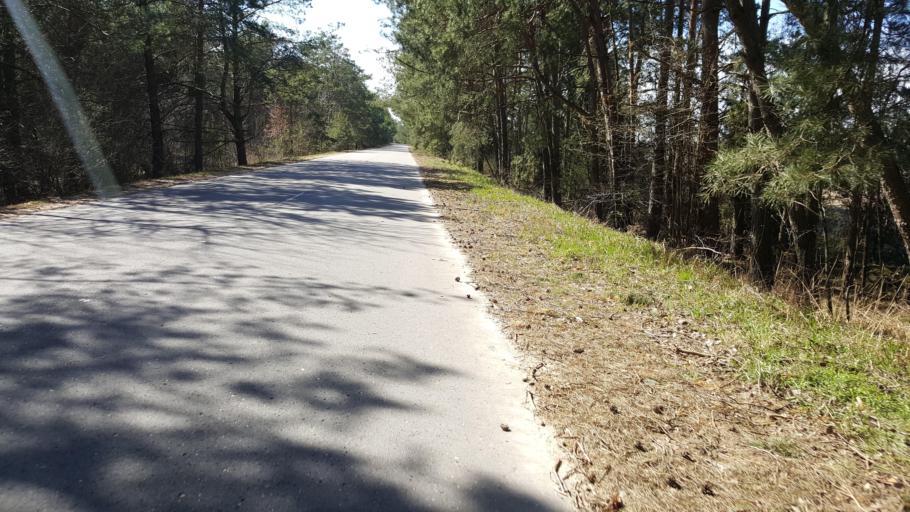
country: BY
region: Brest
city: Kamyanyets
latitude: 52.3075
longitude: 23.8656
